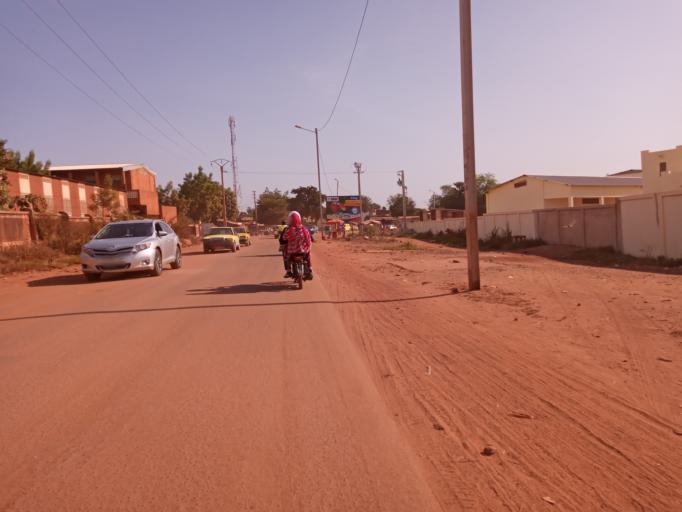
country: ML
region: Bamako
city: Bamako
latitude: 12.6233
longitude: -7.9547
